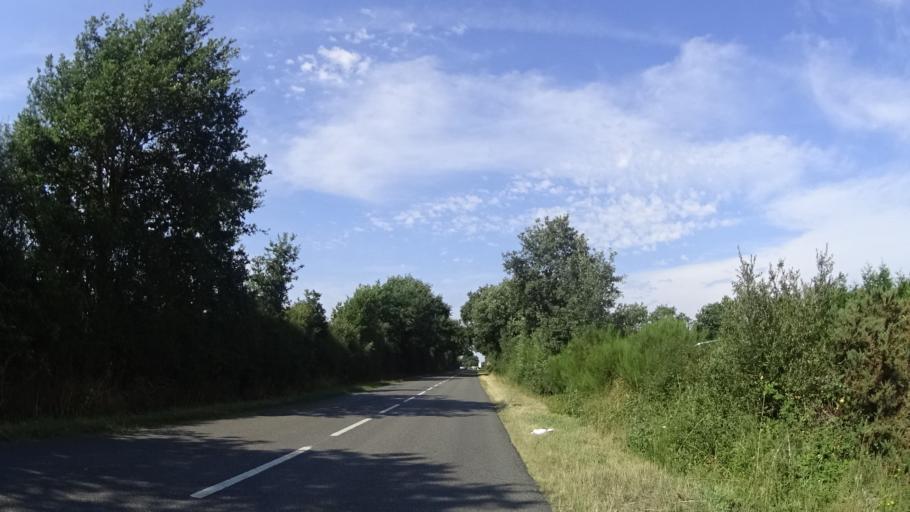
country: FR
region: Pays de la Loire
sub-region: Departement de la Loire-Atlantique
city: Saffre
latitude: 47.5103
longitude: -1.5532
